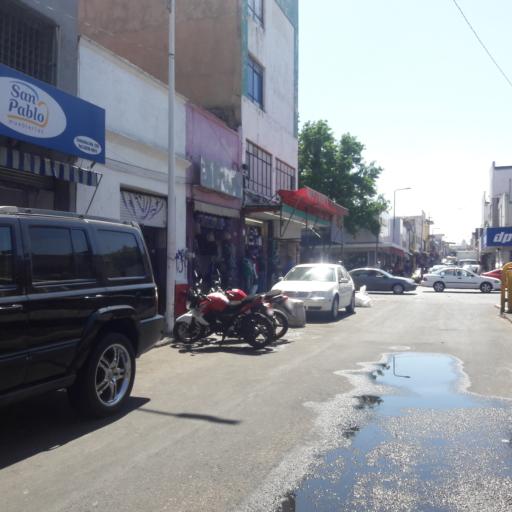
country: MX
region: Jalisco
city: Guadalajara
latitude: 20.6750
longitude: -103.3384
